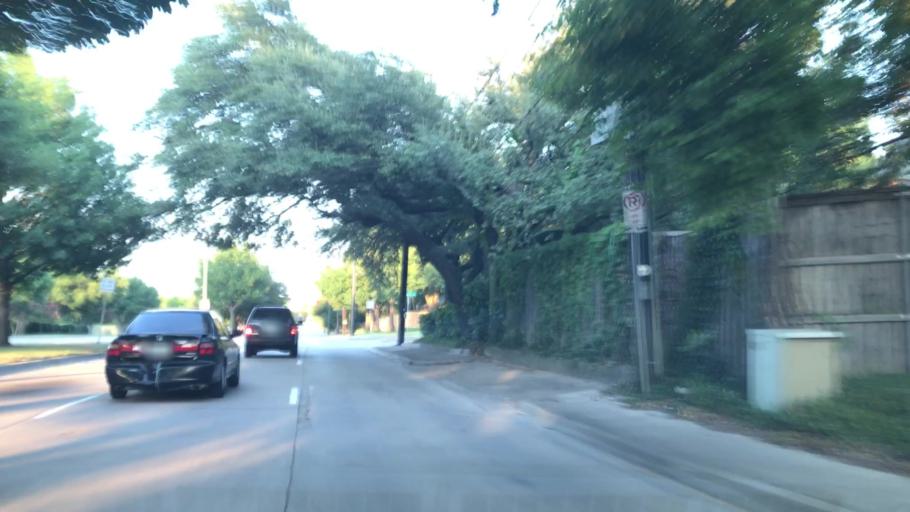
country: US
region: Texas
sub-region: Dallas County
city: University Park
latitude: 32.9096
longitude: -96.7795
